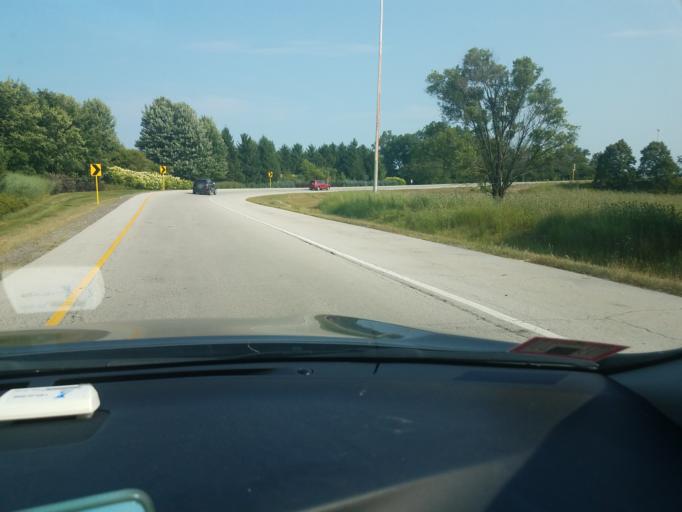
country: US
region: Illinois
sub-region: Cook County
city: Glencoe
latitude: 42.1391
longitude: -87.7874
